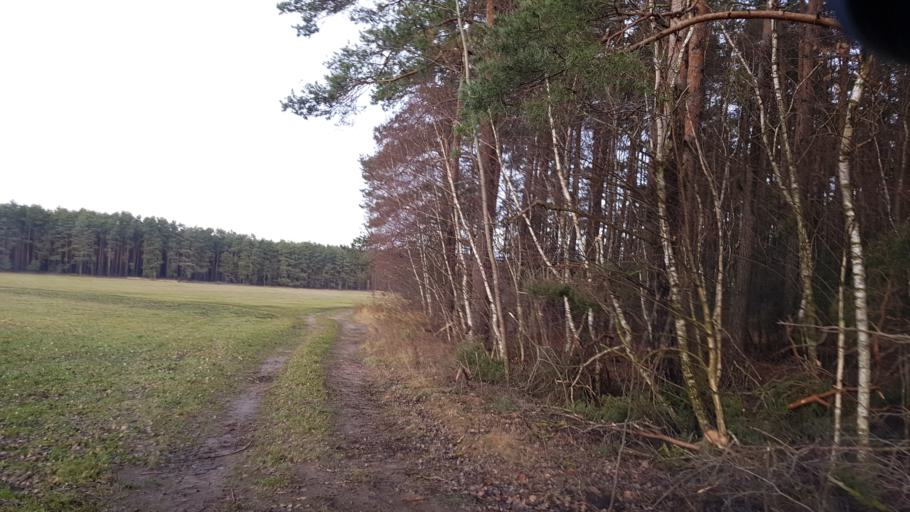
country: DE
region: Brandenburg
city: Sallgast
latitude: 51.6483
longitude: 13.8448
